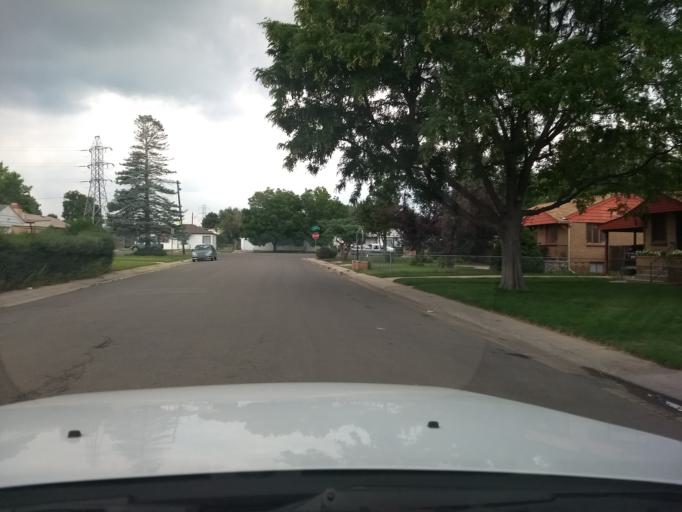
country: US
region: Colorado
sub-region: Denver County
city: Denver
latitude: 39.6991
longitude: -105.0149
